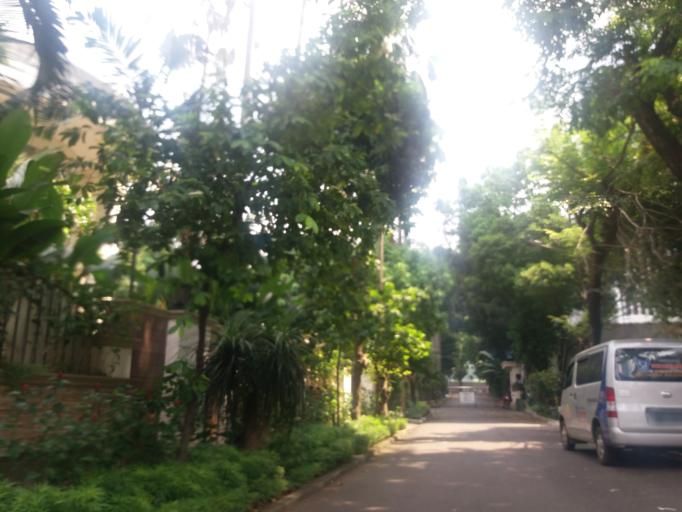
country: ID
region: Jakarta Raya
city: Jakarta
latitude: -6.2258
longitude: 106.8287
